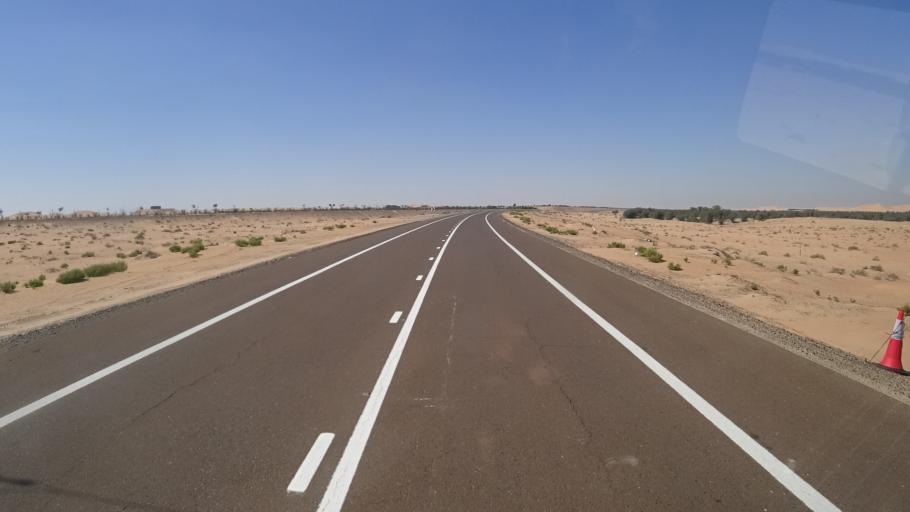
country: AE
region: Abu Dhabi
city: Al Ain
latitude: 24.1204
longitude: 55.1849
